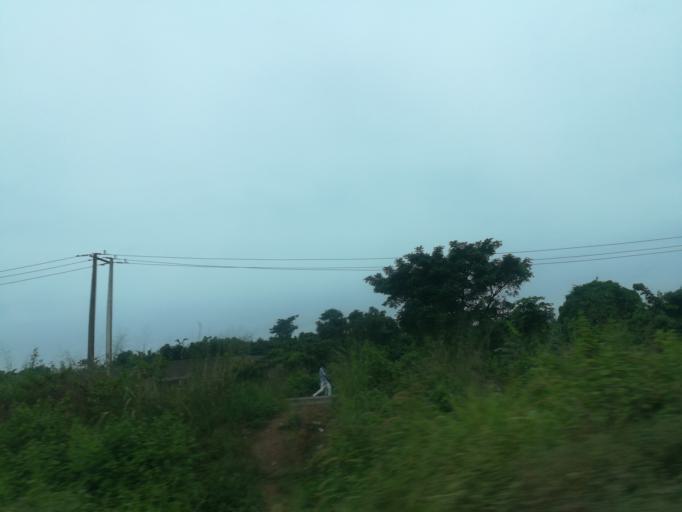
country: NG
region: Oyo
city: Egbeda
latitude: 7.3810
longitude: 4.0006
